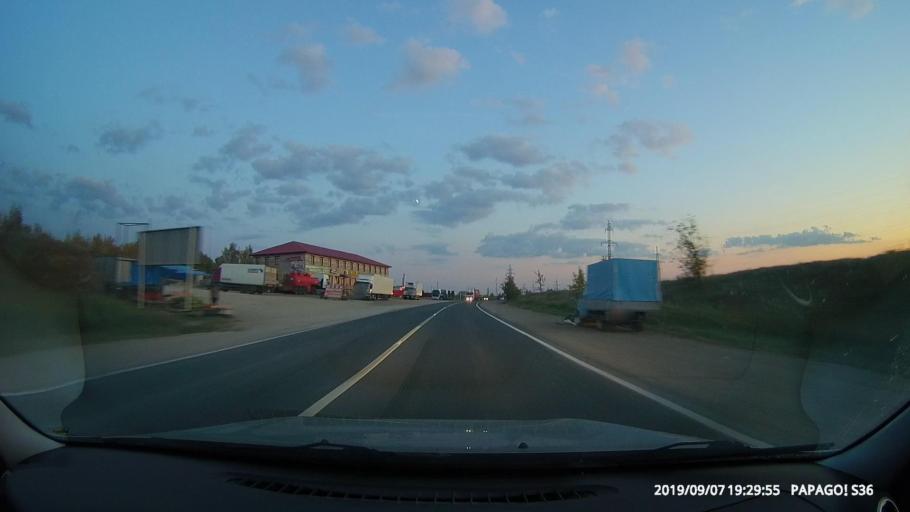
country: RU
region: Samara
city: Chapayevsk
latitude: 52.9974
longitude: 49.7679
